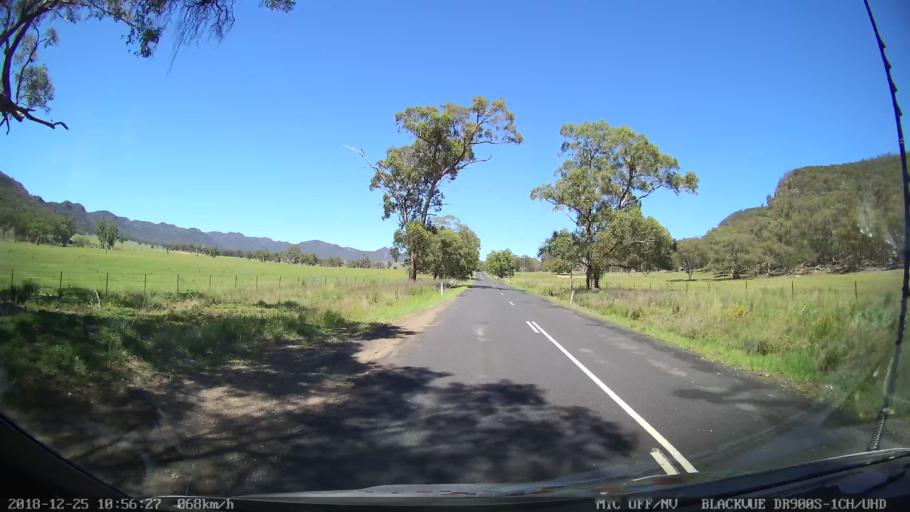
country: AU
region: New South Wales
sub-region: Upper Hunter Shire
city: Merriwa
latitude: -32.4013
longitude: 150.2626
